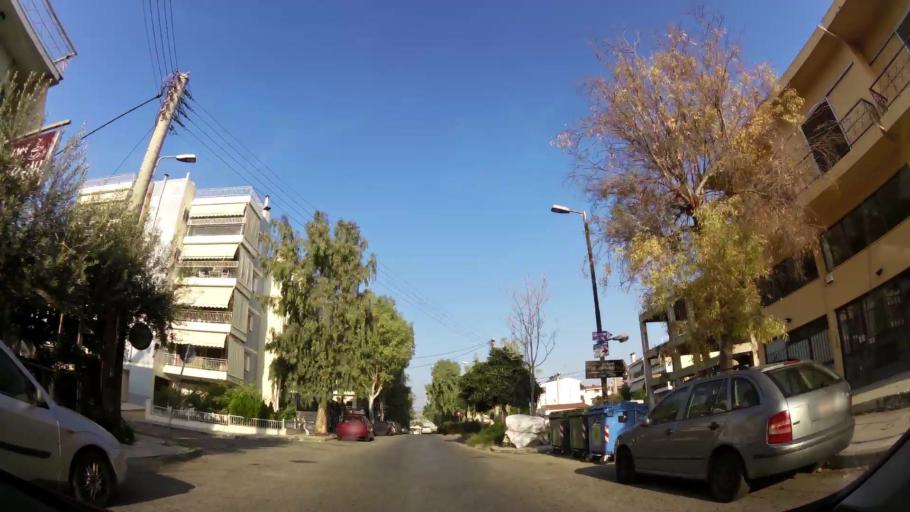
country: GR
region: Attica
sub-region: Nomarchia Athinas
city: Nea Filadelfeia
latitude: 38.0441
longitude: 23.7322
